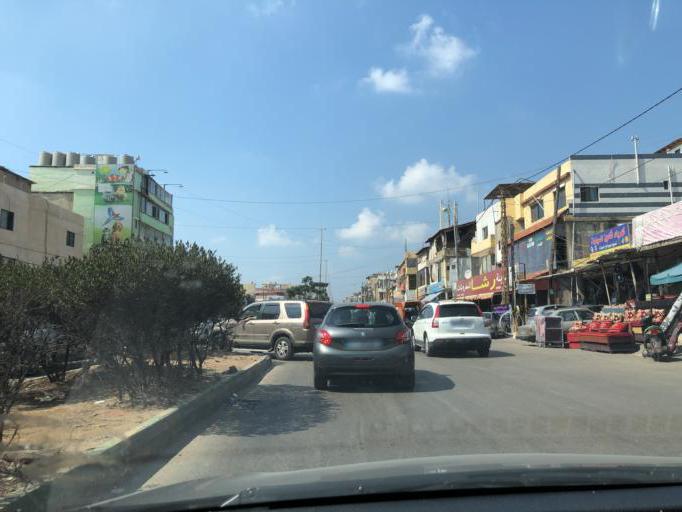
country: LB
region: Beyrouth
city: Beirut
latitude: 33.8401
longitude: 35.4847
